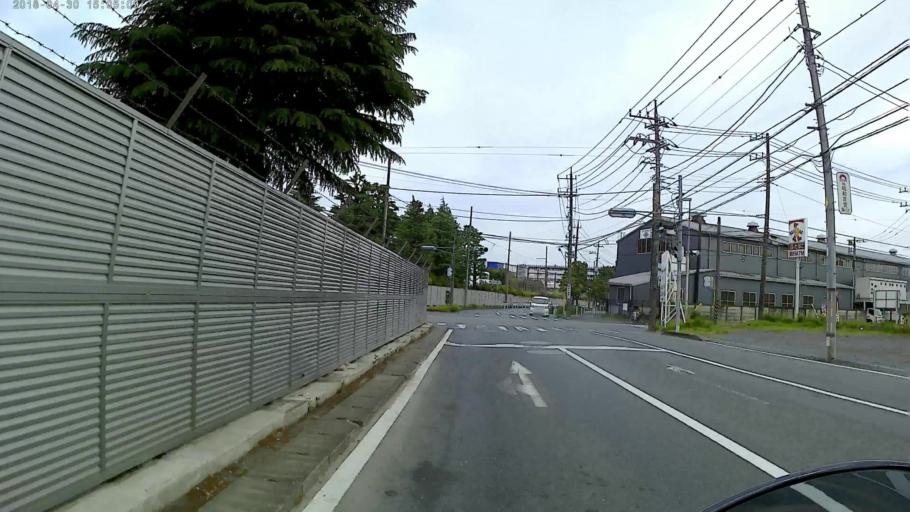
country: JP
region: Kanagawa
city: Zama
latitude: 35.5614
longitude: 139.3394
